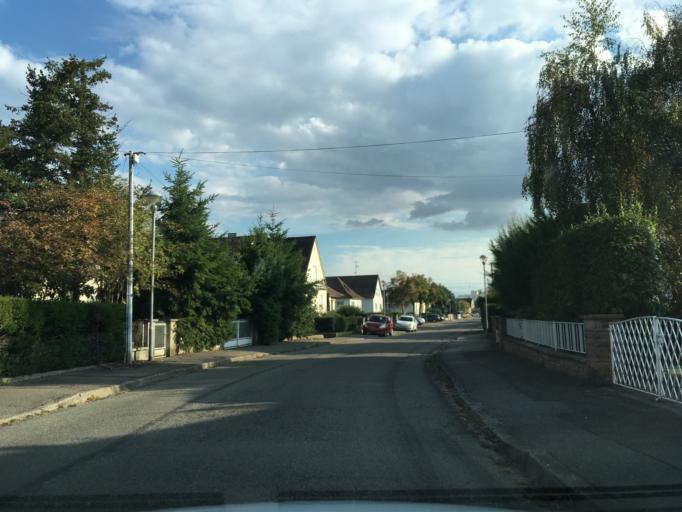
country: FR
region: Alsace
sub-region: Departement du Haut-Rhin
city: Colmar
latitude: 48.0904
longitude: 7.3466
